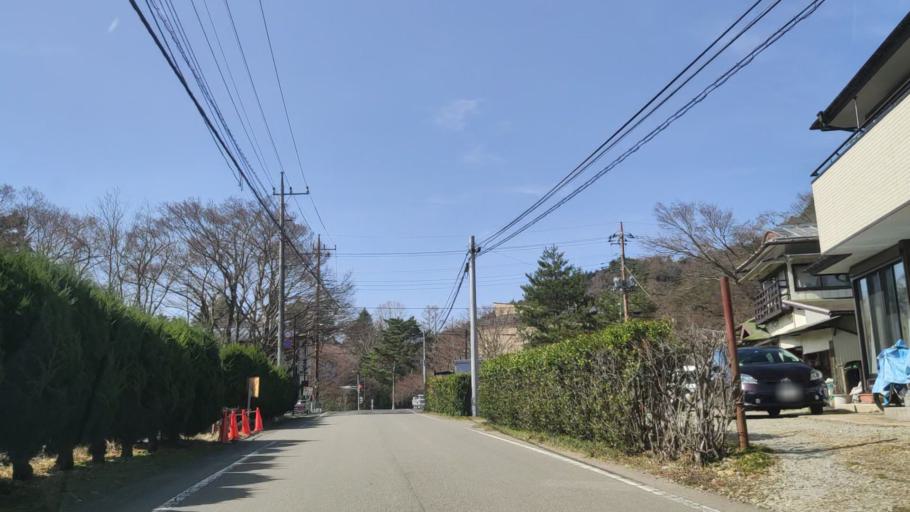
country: JP
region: Yamanashi
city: Fujikawaguchiko
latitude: 35.5265
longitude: 138.7620
